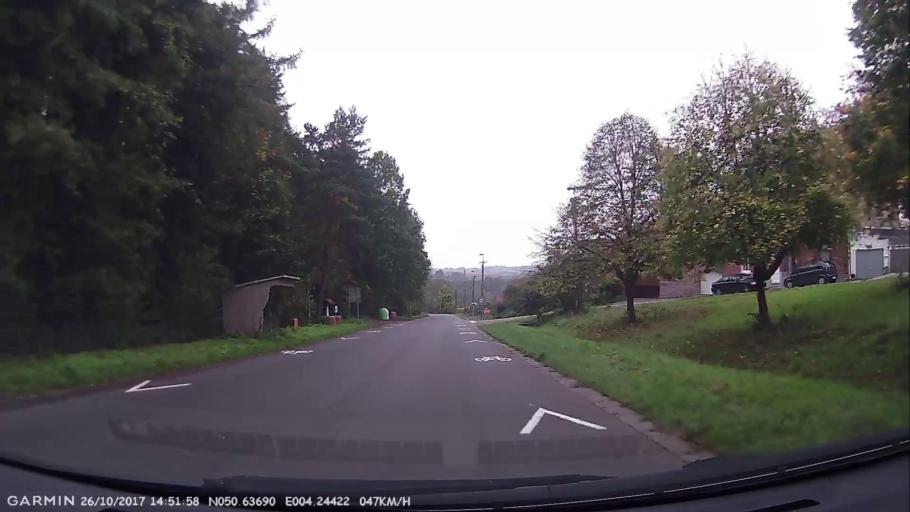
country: BE
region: Wallonia
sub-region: Province du Brabant Wallon
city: Ittre
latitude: 50.6370
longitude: 4.2441
